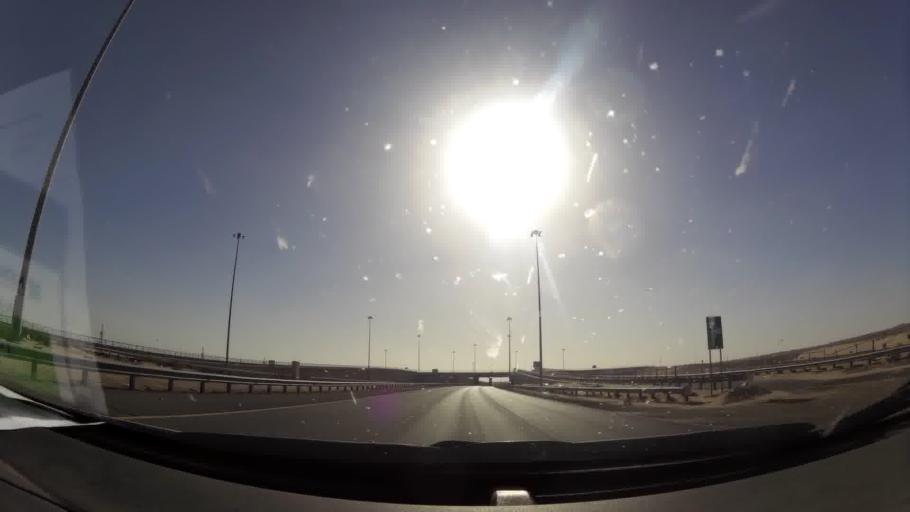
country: KW
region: Al Asimah
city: Kuwait City
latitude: 29.5761
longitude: 47.9023
